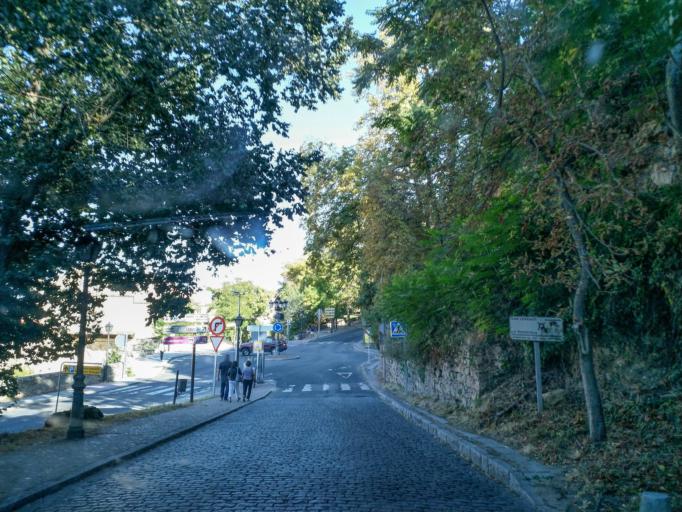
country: ES
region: Castille and Leon
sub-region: Provincia de Segovia
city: Segovia
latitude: 40.9525
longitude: -4.1204
